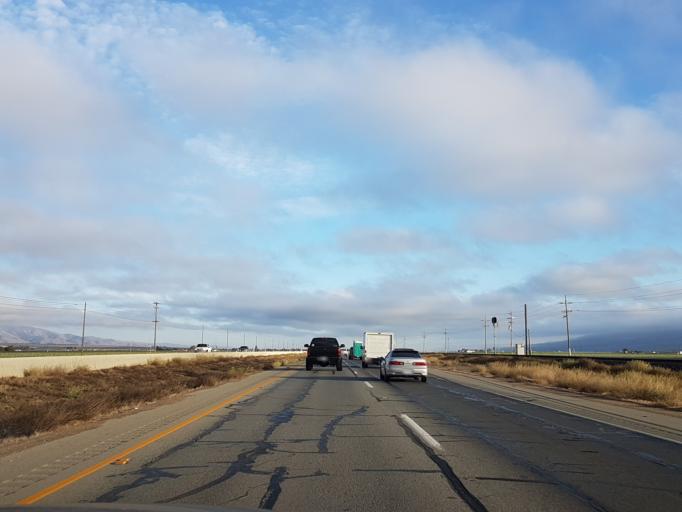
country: US
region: California
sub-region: Monterey County
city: Chualar
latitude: 36.5426
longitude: -121.4889
